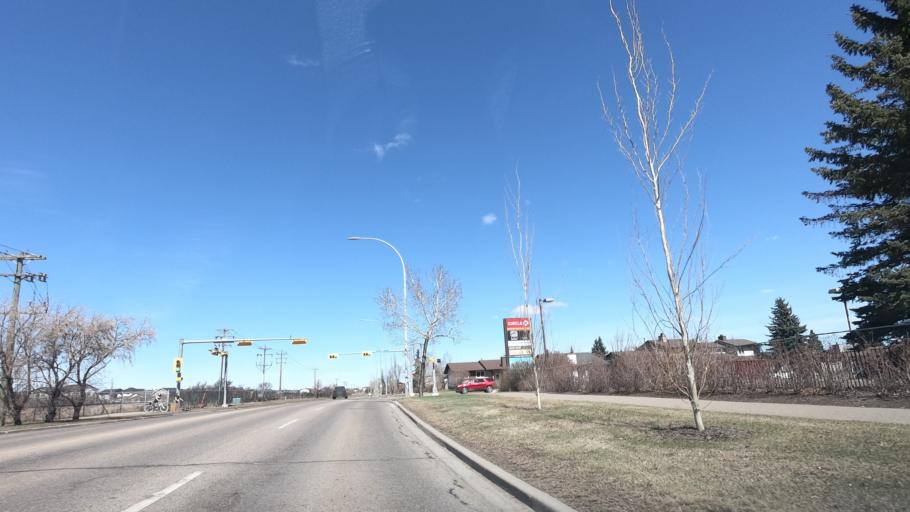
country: CA
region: Alberta
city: Airdrie
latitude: 51.2732
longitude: -114.0124
